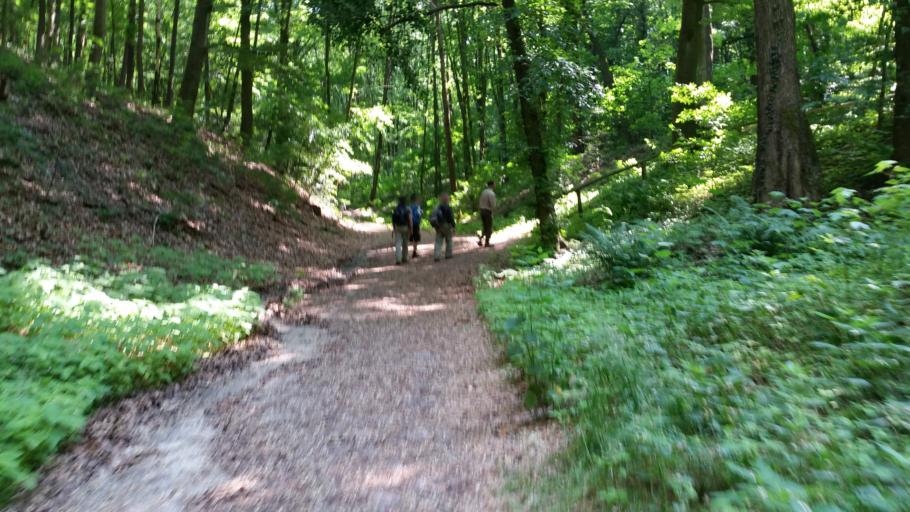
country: DE
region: Brandenburg
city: Reitwein
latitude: 52.4961
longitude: 14.5670
